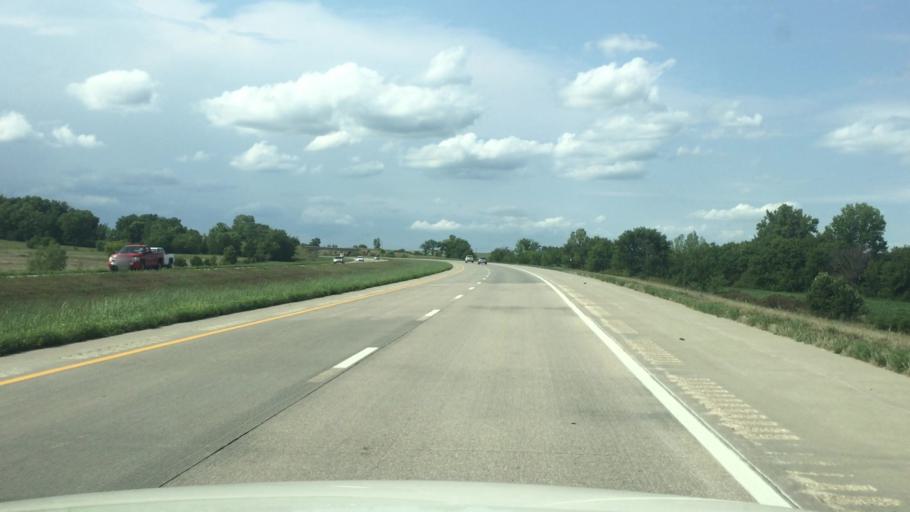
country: US
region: Kansas
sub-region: Miami County
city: Louisburg
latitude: 38.5417
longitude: -94.6848
